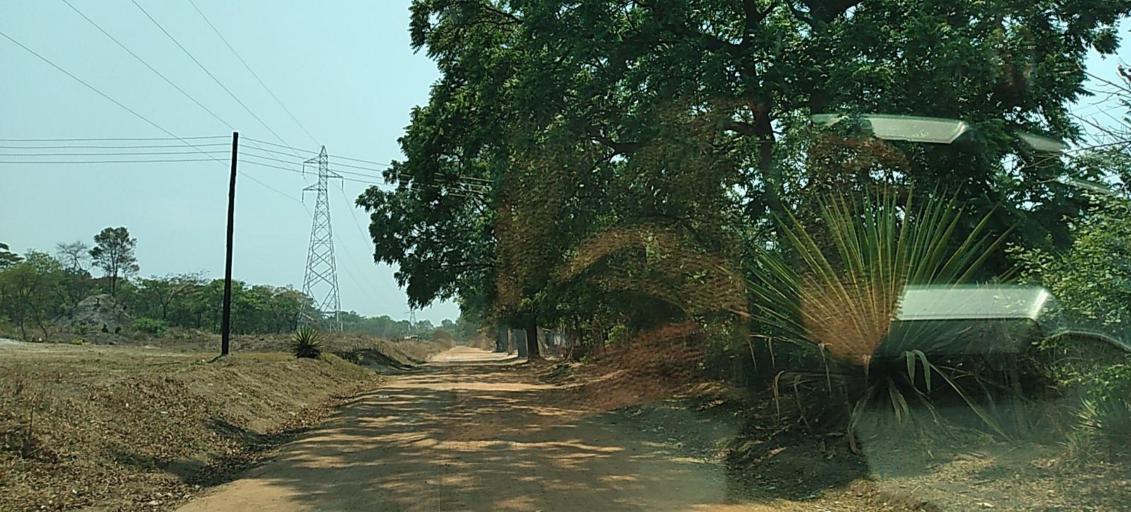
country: ZM
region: Copperbelt
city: Chambishi
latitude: -12.6202
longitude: 27.9468
